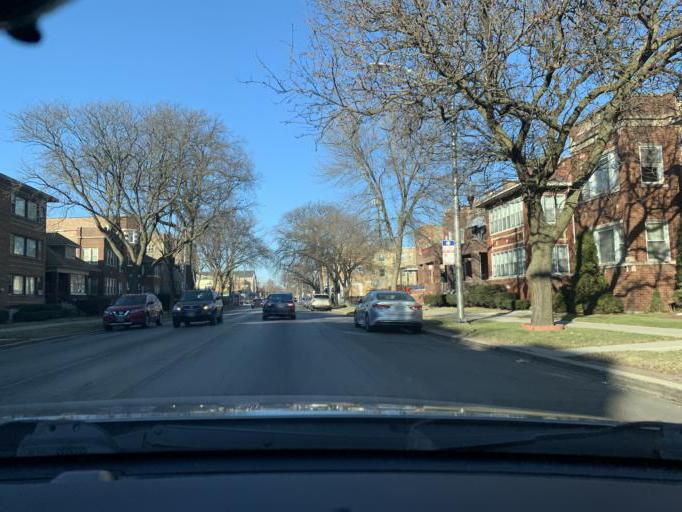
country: US
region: Illinois
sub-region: Cook County
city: Oak Park
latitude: 41.8786
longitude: -87.7746
